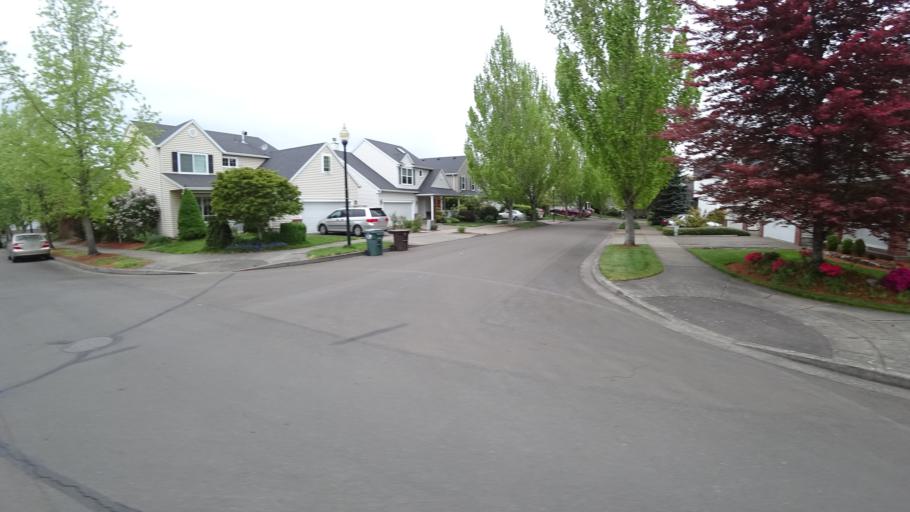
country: US
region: Oregon
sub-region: Washington County
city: Hillsboro
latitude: 45.5417
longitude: -122.9717
